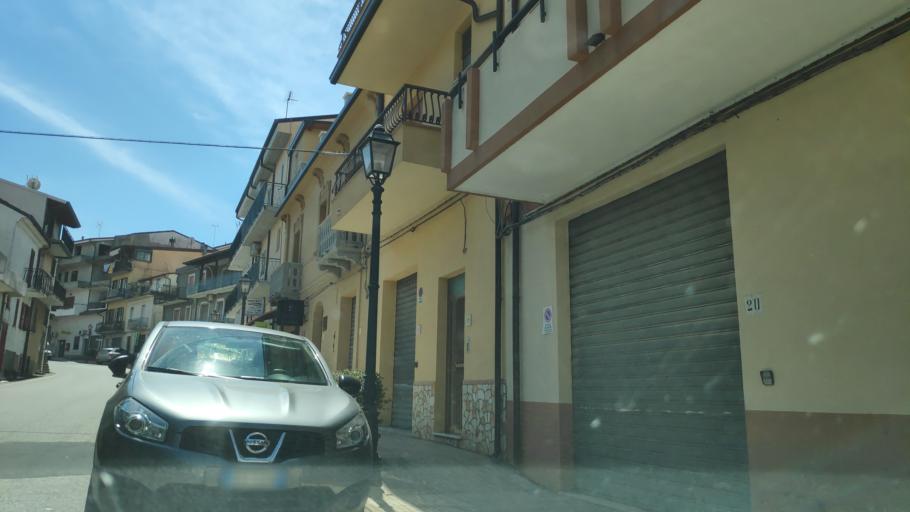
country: IT
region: Calabria
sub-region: Provincia di Catanzaro
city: Palermiti
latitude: 38.7505
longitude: 16.4531
